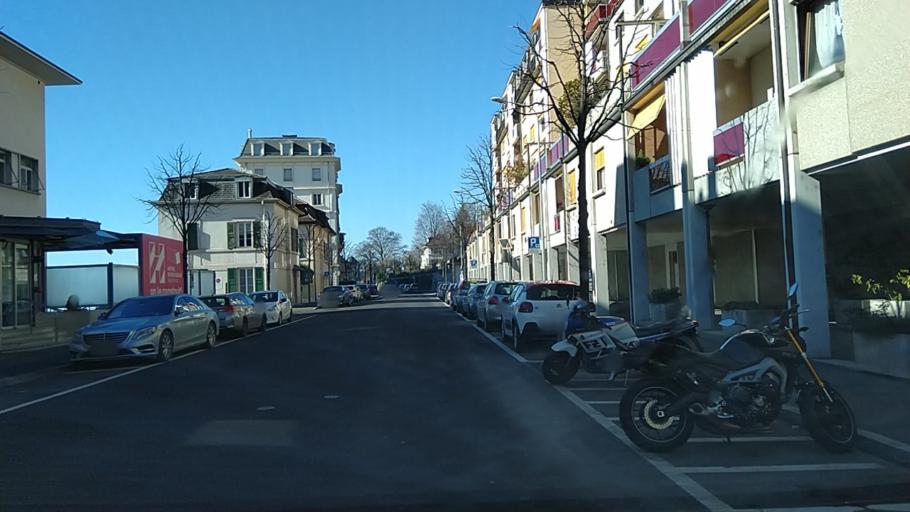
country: CH
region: Vaud
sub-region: Riviera-Pays-d'Enhaut District
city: Montreux
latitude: 46.4402
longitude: 6.9083
